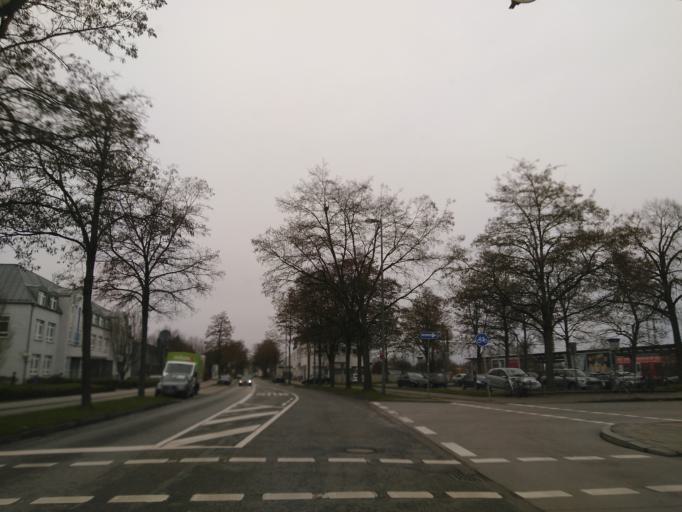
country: DE
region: Bavaria
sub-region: Upper Bavaria
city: Neubiberg
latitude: 48.1256
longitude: 11.6629
